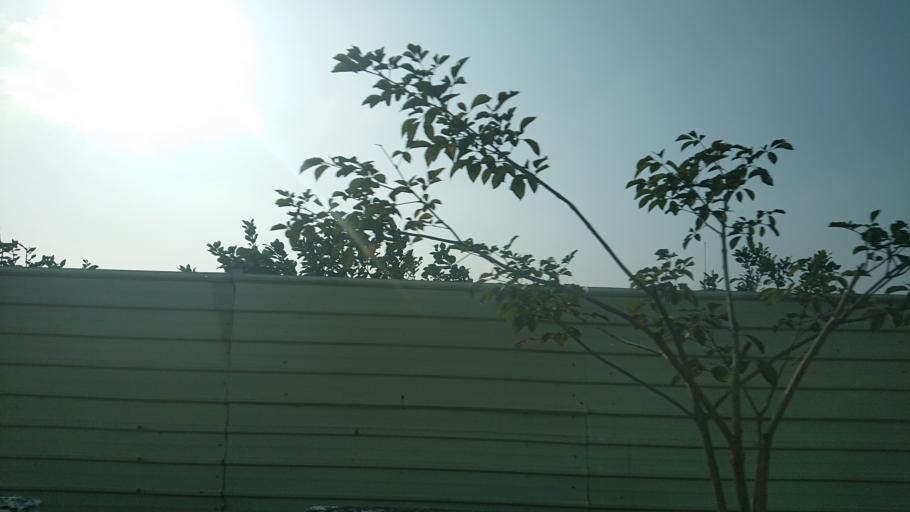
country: TW
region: Taiwan
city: Xinying
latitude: 23.2026
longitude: 120.2711
